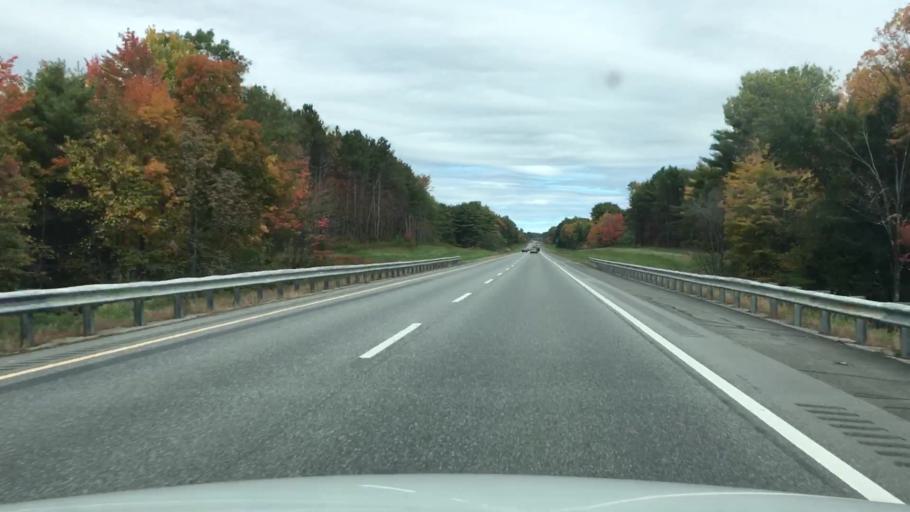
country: US
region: Maine
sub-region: Kennebec County
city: Sidney
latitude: 44.4339
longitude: -69.7312
